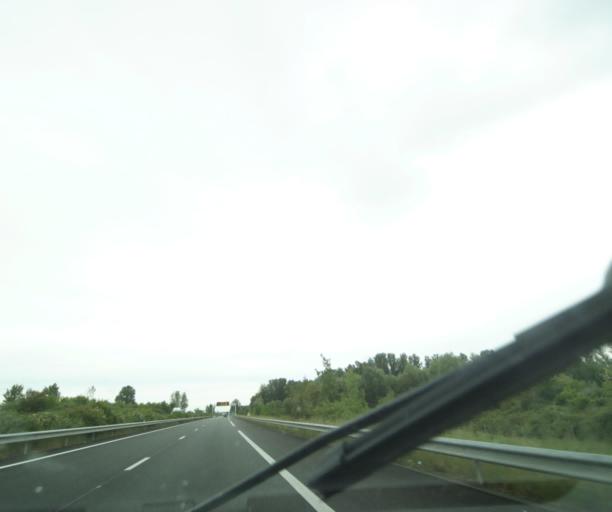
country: FR
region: Midi-Pyrenees
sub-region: Departement du Tarn-et-Garonne
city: Realville
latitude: 44.1305
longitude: 1.4845
